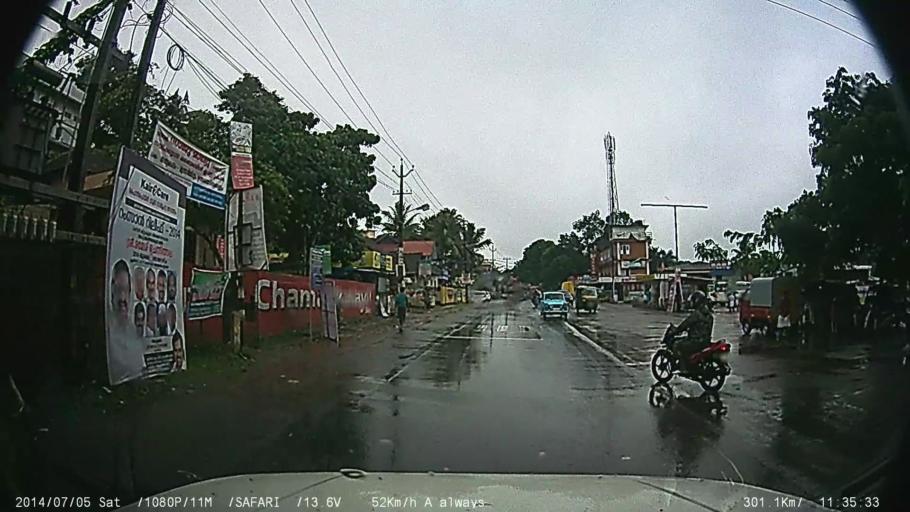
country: IN
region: Kerala
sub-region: Ernakulam
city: Muvattupula
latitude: 9.9791
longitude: 76.5866
